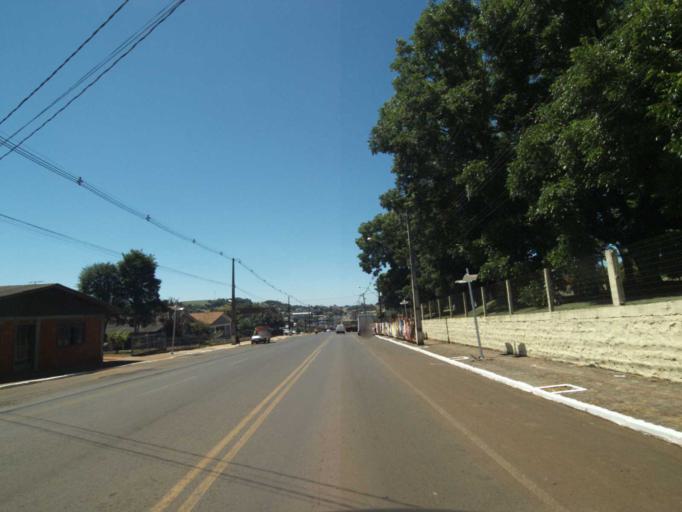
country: BR
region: Parana
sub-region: Coronel Vivida
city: Coronel Vivida
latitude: -25.9738
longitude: -52.8138
